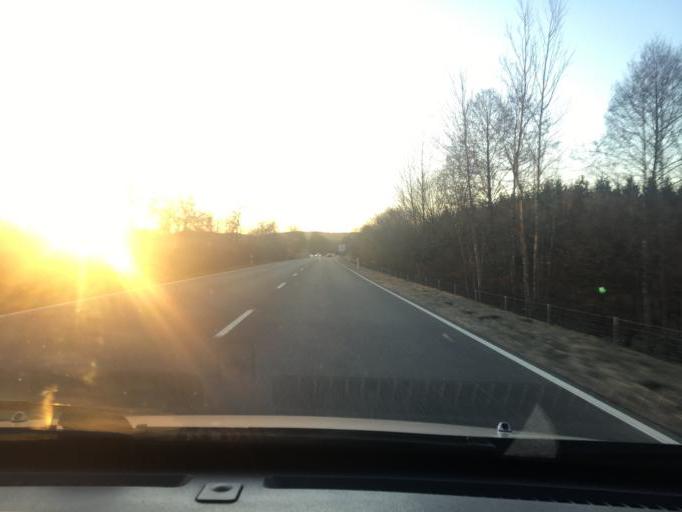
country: DE
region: Baden-Wuerttemberg
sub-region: Tuebingen Region
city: Berkheim
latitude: 48.0499
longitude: 10.0626
